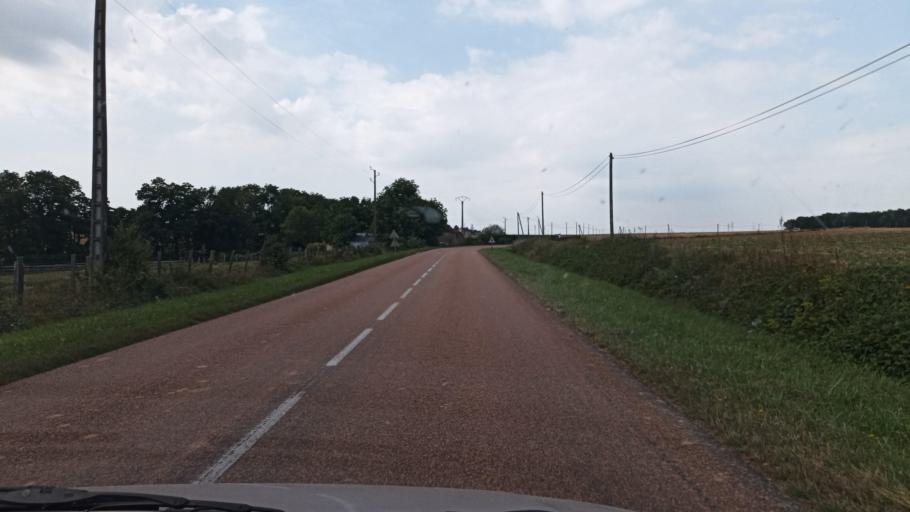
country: FR
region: Bourgogne
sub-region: Departement de l'Yonne
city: Villeneuve-sur-Yonne
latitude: 48.0620
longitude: 3.2532
